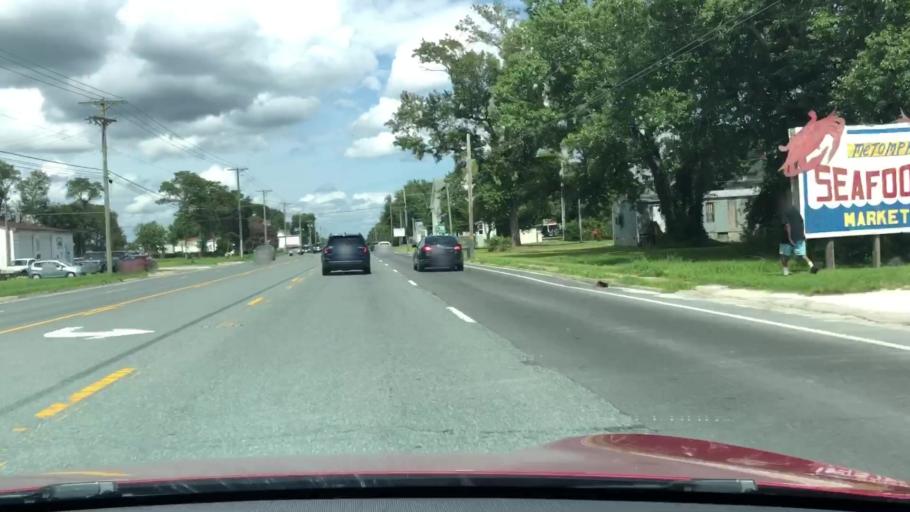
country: US
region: Virginia
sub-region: Accomack County
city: Wattsville
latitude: 37.8442
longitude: -75.5682
